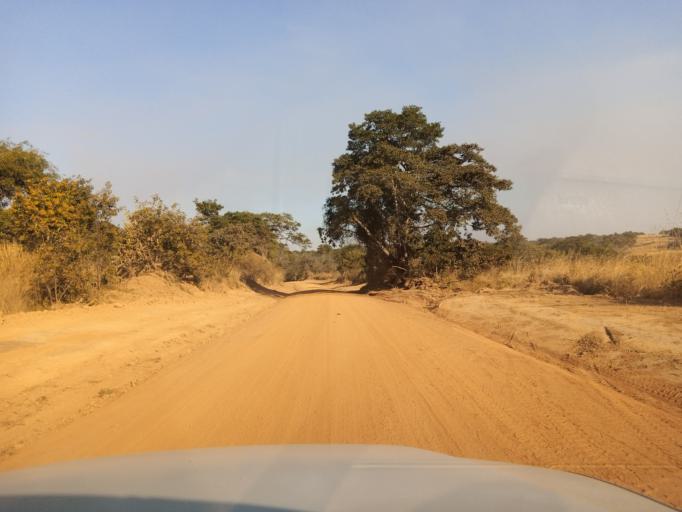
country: CD
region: Katanga
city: Lubumbashi
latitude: -11.3010
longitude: 27.2807
